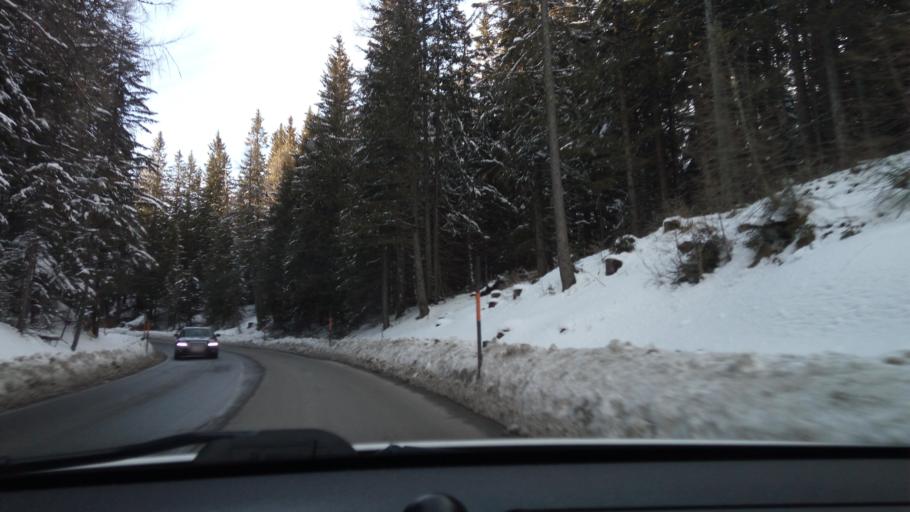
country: AT
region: Salzburg
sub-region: Politischer Bezirk Tamsweg
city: Sankt Michael im Lungau
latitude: 47.0569
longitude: 13.6173
